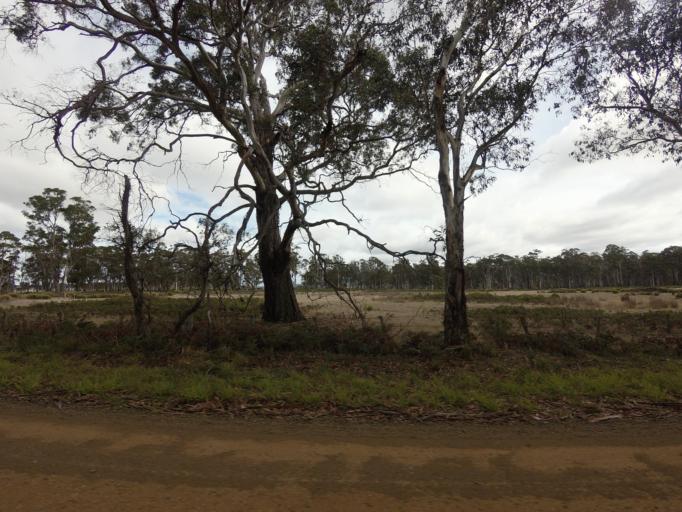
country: AU
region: Tasmania
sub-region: Brighton
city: Bridgewater
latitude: -42.4226
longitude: 147.4241
